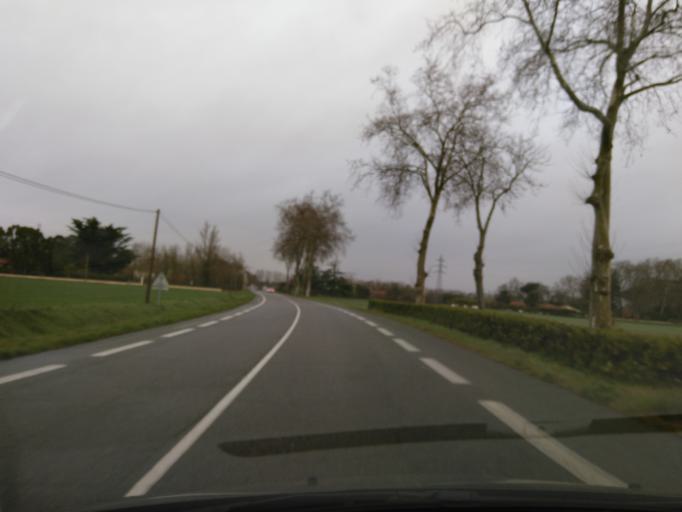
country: FR
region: Midi-Pyrenees
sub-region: Departement de la Haute-Garonne
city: Carbonne
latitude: 43.2856
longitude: 1.2169
